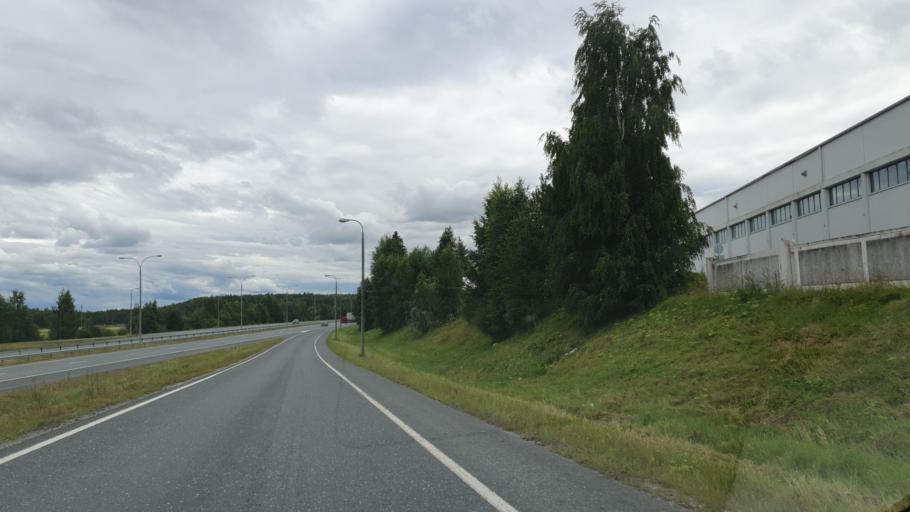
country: FI
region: Northern Savo
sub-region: Ylae-Savo
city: Iisalmi
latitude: 63.5236
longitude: 27.2489
